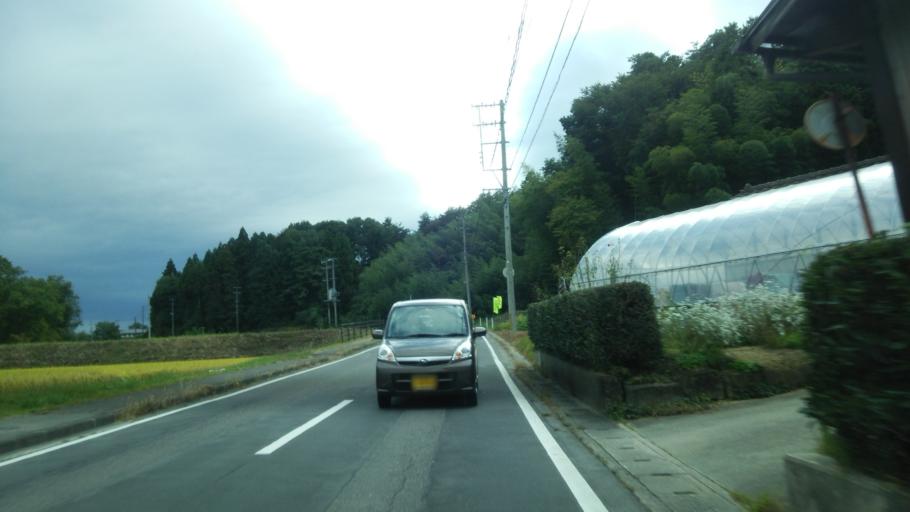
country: JP
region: Fukushima
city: Sukagawa
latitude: 37.3054
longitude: 140.2865
